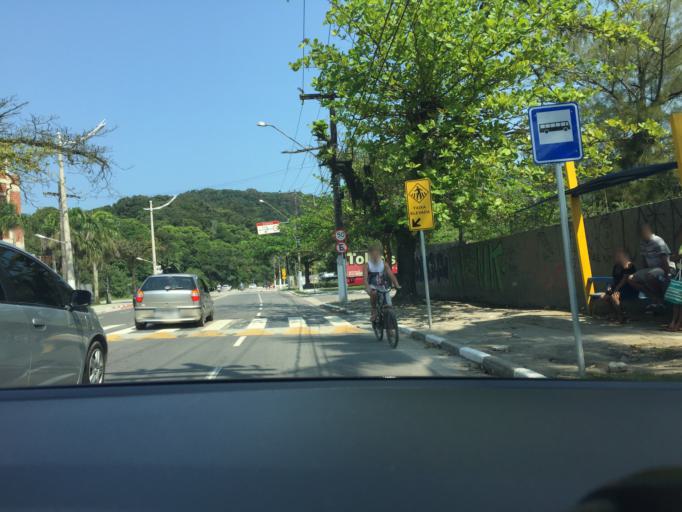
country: BR
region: Sao Paulo
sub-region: Guaruja
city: Guaruja
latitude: -23.9737
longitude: -46.1892
